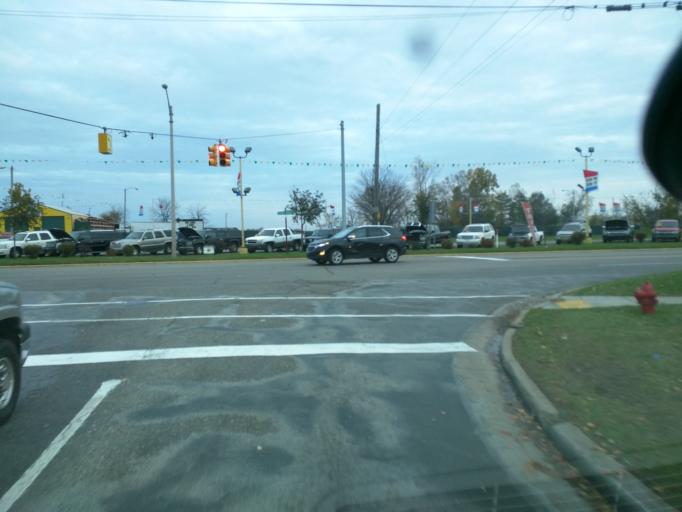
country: US
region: Michigan
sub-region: Ingham County
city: Edgemont Park
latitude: 42.7693
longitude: -84.6006
